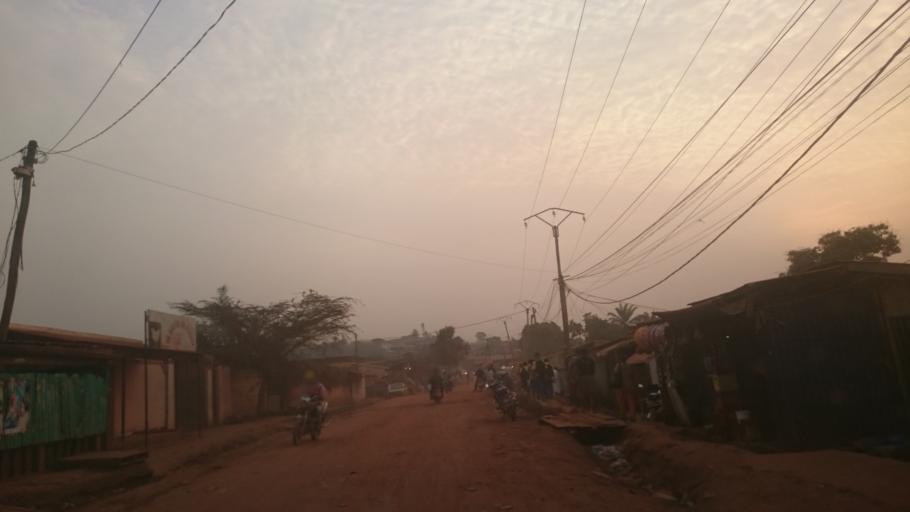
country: CM
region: Centre
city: Yaounde
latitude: 3.8203
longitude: 11.5070
